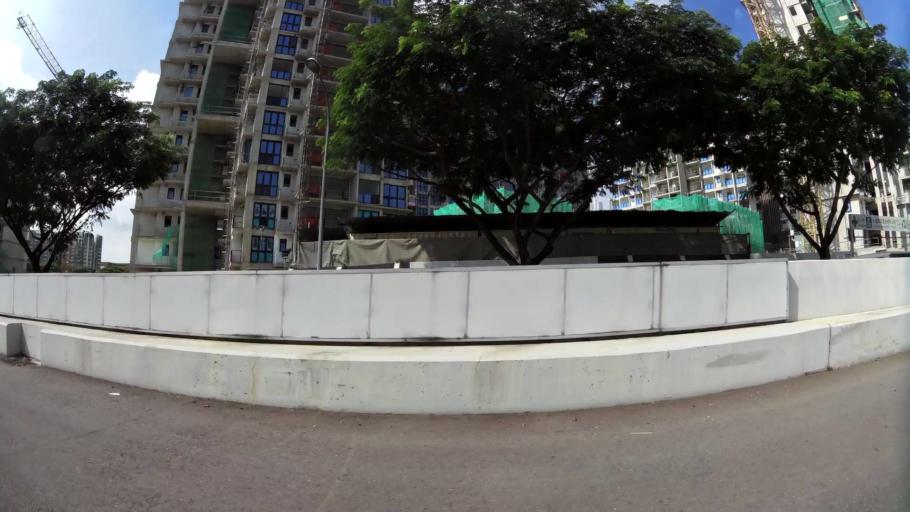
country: SG
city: Singapore
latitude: 1.3427
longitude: 103.8831
